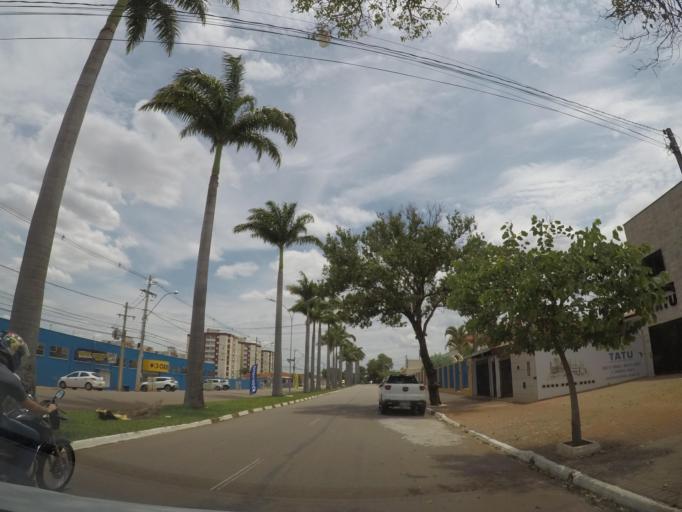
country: BR
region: Sao Paulo
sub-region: Sumare
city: Sumare
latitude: -22.8327
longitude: -47.2656
